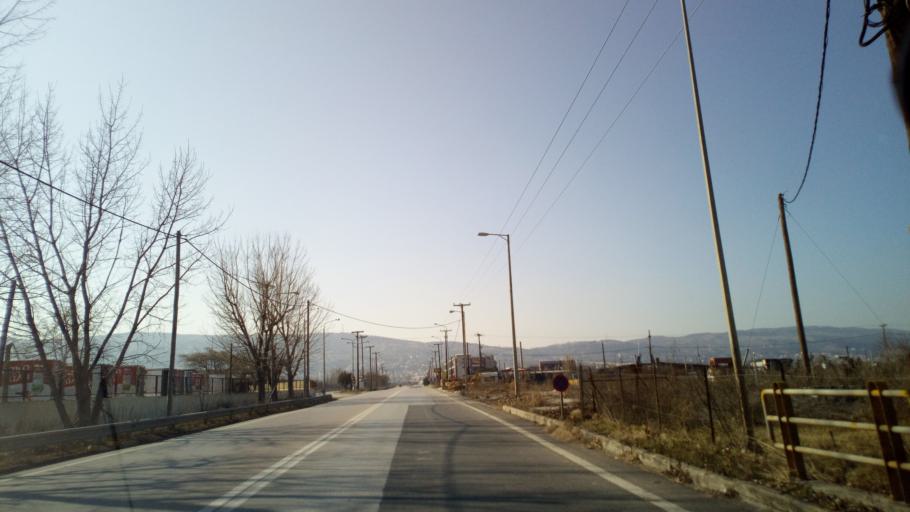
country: GR
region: Central Macedonia
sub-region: Nomos Thessalonikis
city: Lagyna
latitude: 40.7331
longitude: 23.0254
